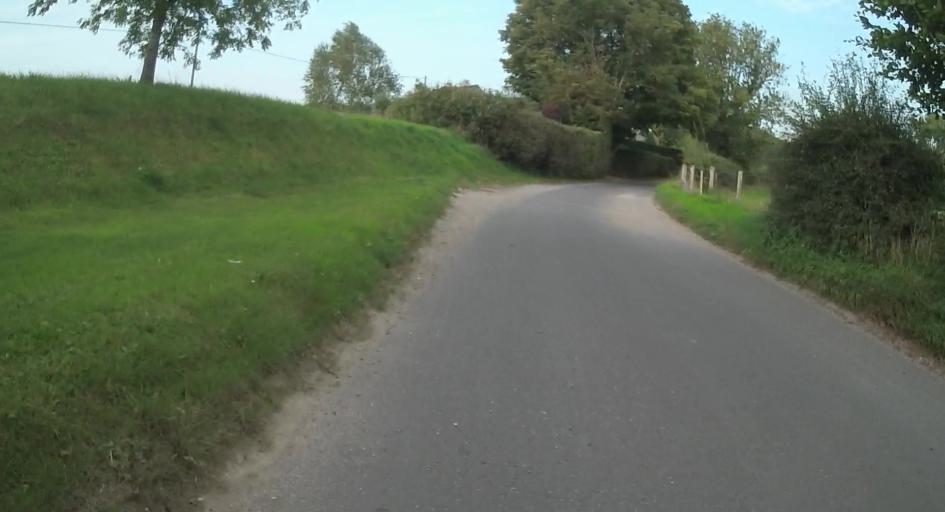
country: GB
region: England
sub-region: Hampshire
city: Kings Worthy
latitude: 51.0707
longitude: -1.1859
